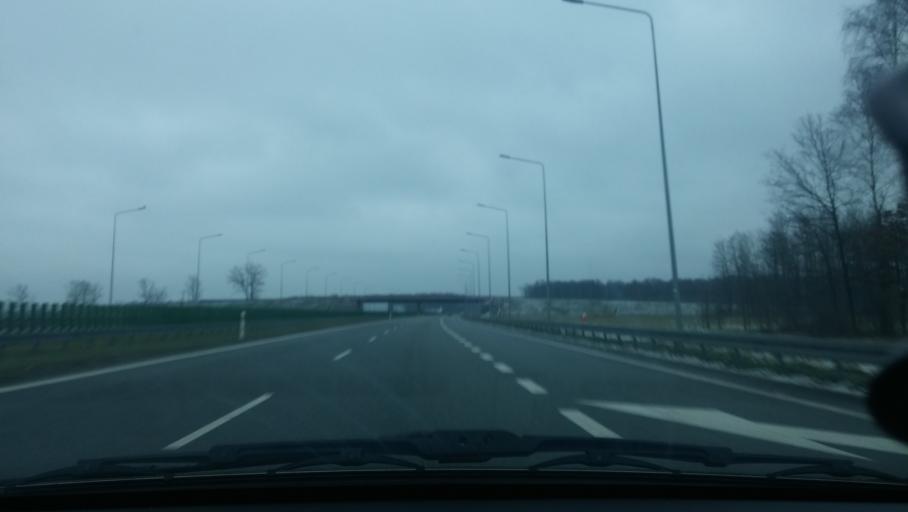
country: PL
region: Masovian Voivodeship
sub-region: Powiat minski
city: Jakubow
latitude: 52.2142
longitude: 21.6479
